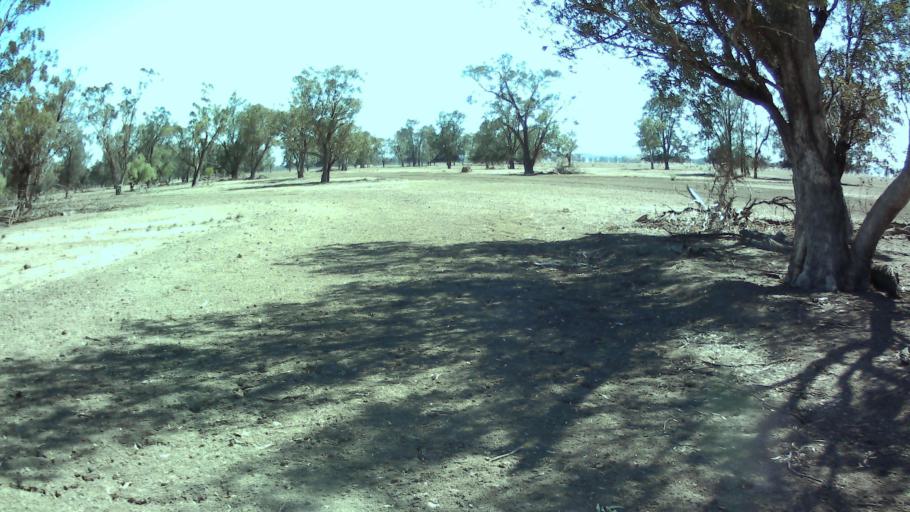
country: AU
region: New South Wales
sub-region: Bland
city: West Wyalong
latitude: -33.7643
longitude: 147.6581
